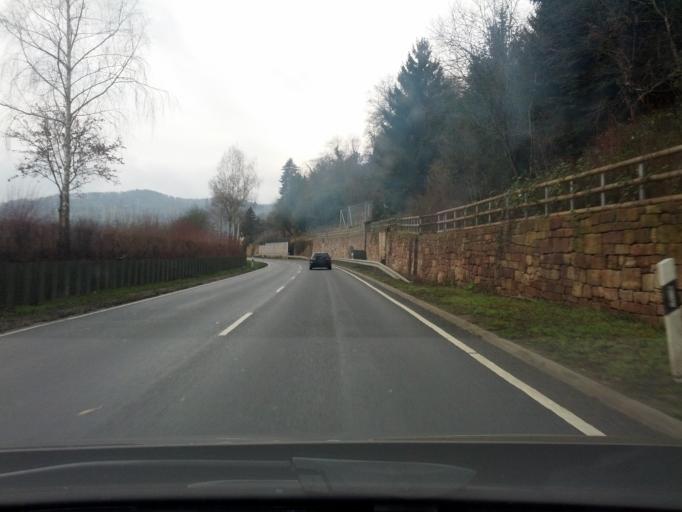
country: DE
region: Hesse
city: Witzenhausen
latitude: 51.3502
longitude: 9.8652
